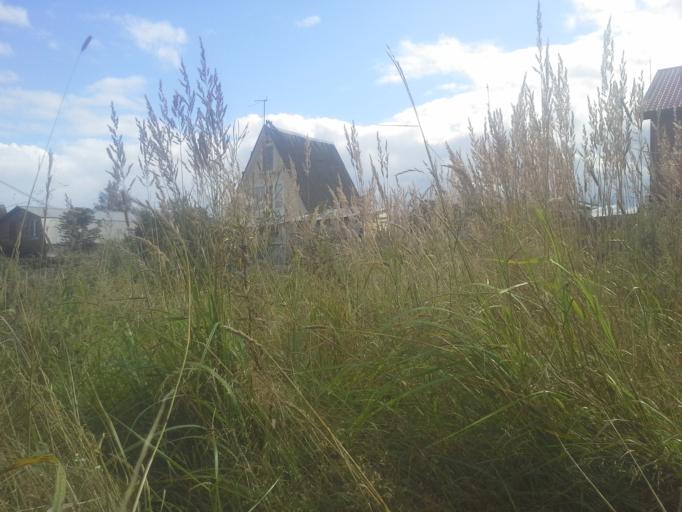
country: RU
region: Moskovskaya
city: Kievskij
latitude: 55.3526
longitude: 36.9586
